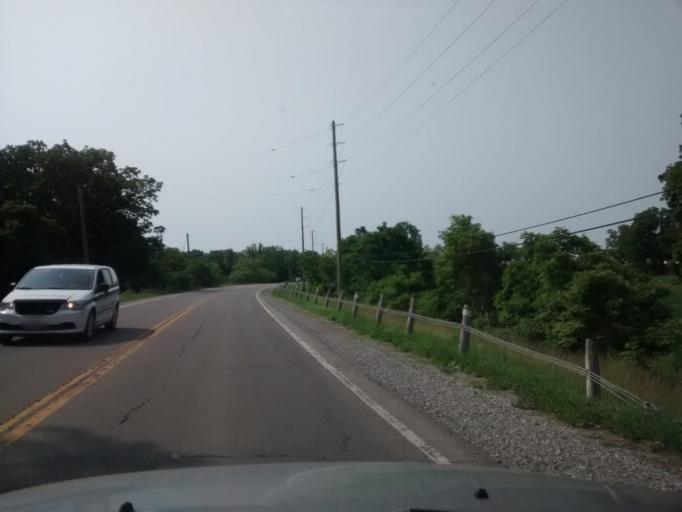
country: CA
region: Ontario
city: Ancaster
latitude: 43.0412
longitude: -79.9028
